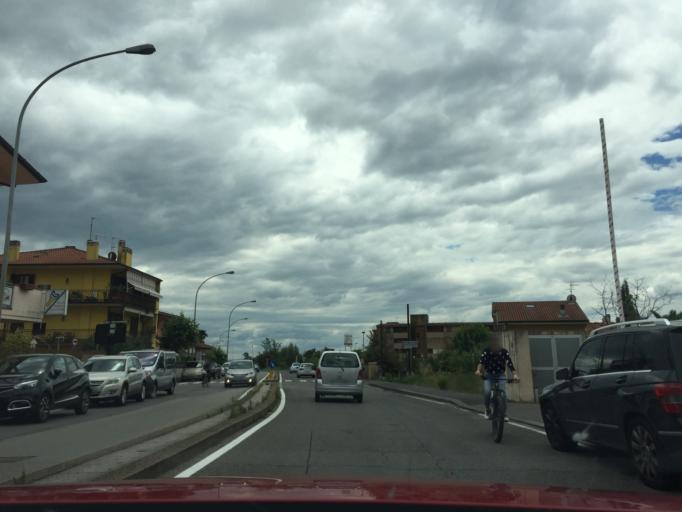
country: IT
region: Tuscany
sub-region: Provincia di Pistoia
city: Montecatini-Terme
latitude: 43.8780
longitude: 10.7754
